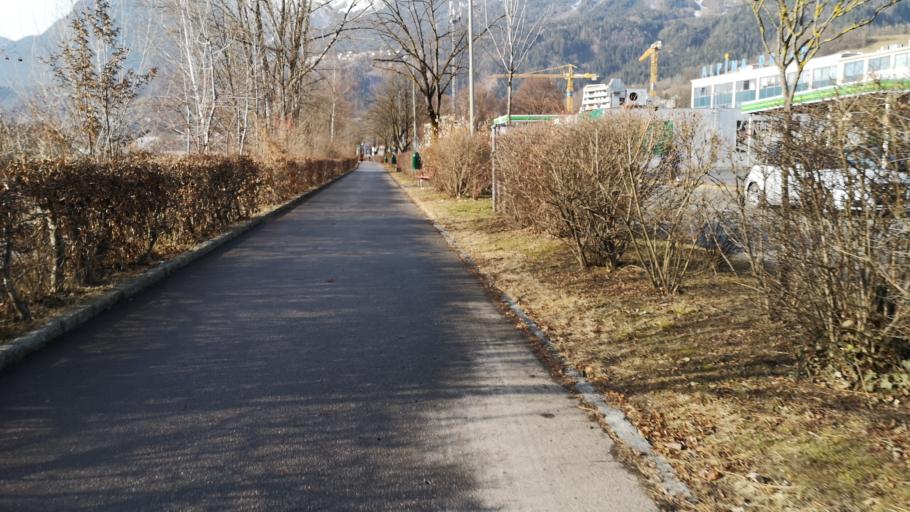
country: AT
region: Tyrol
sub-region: Politischer Bezirk Innsbruck Land
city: Rum
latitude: 47.2770
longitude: 11.4245
